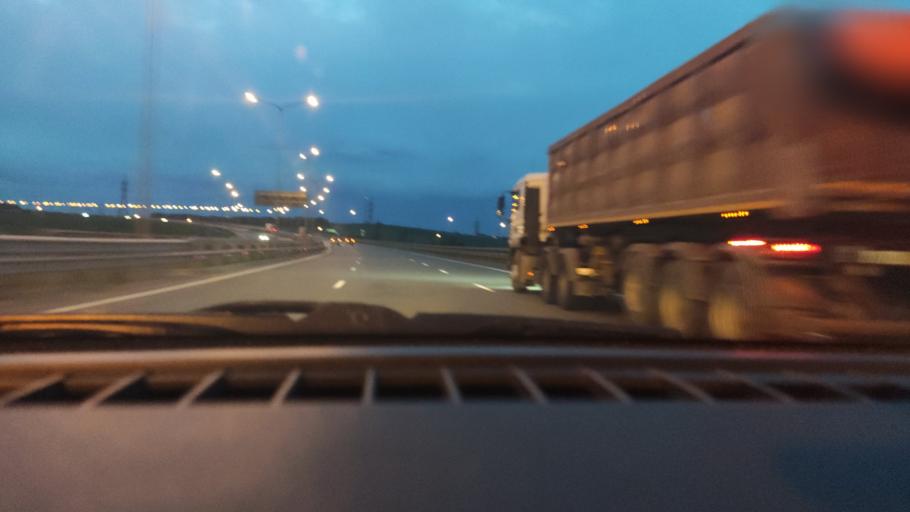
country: RU
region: Perm
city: Lobanovo
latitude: 57.8412
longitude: 56.2971
